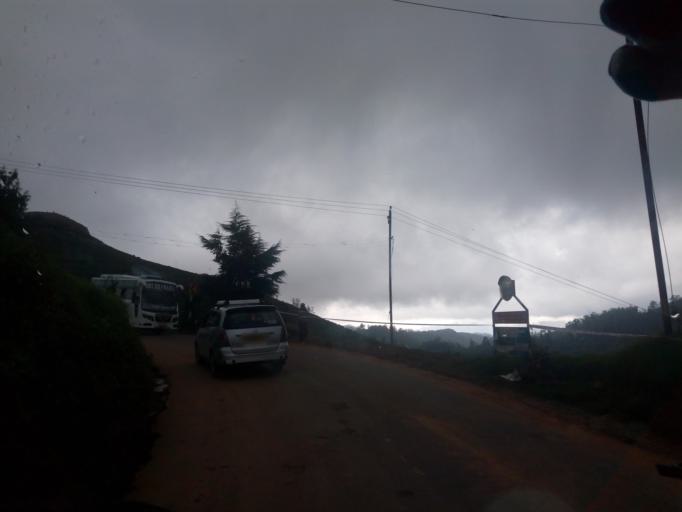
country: IN
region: Tamil Nadu
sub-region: Nilgiri
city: Ooty
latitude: 11.3937
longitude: 76.7170
